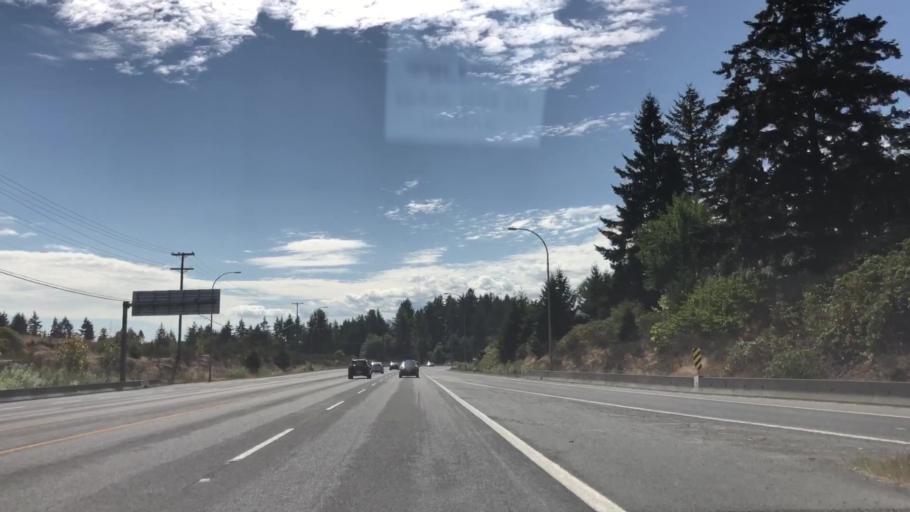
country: CA
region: British Columbia
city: Nanaimo
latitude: 49.1230
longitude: -123.8632
